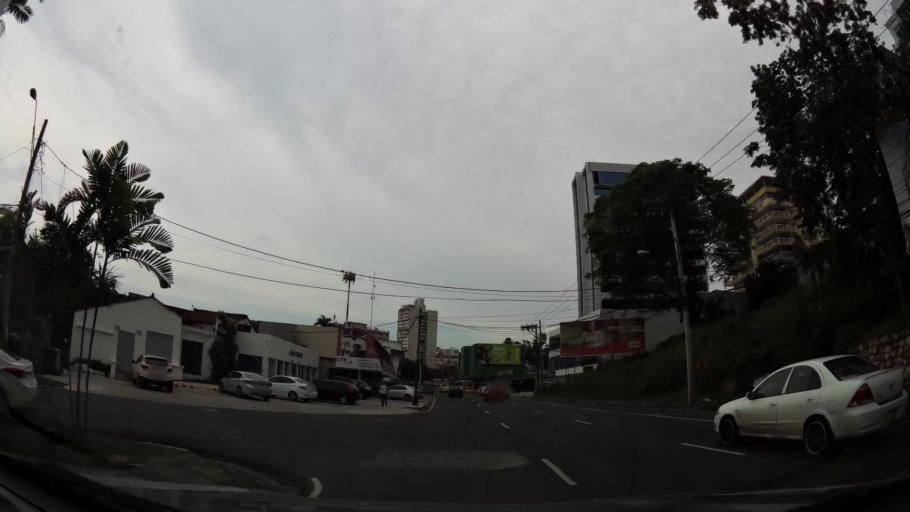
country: PA
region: Panama
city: Panama
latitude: 8.9785
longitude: -79.5318
